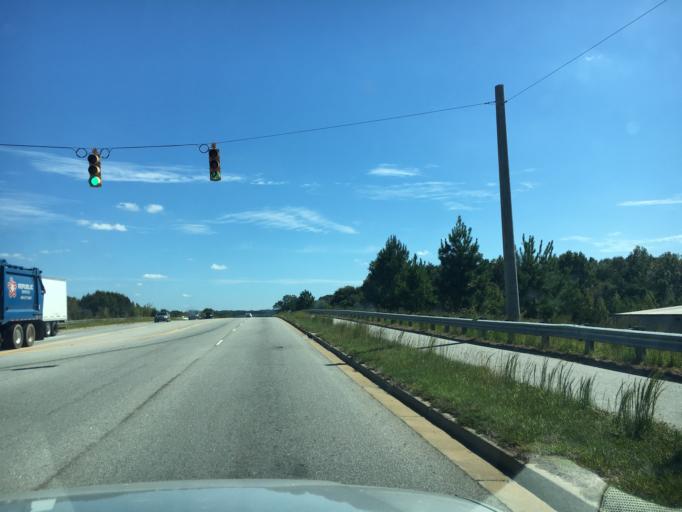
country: US
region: South Carolina
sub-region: Spartanburg County
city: Spartanburg
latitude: 34.9080
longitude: -81.9327
